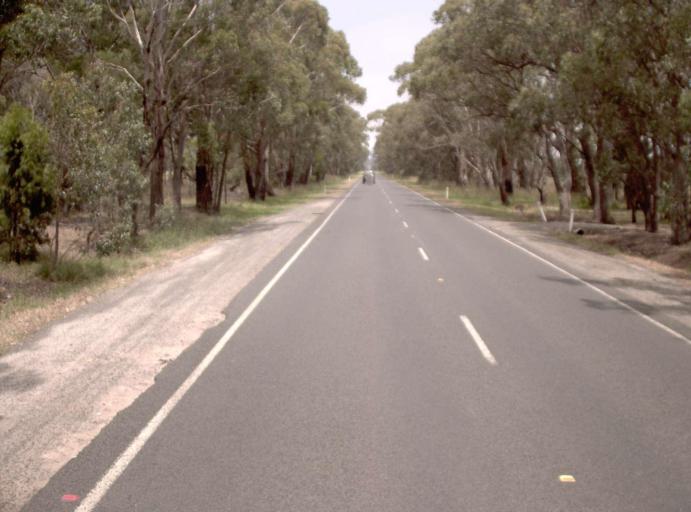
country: AU
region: Victoria
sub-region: Latrobe
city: Traralgon
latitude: -38.4866
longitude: 146.7142
